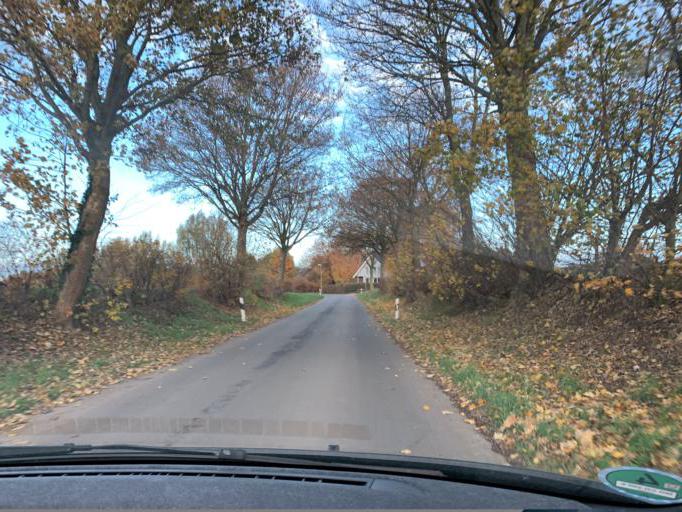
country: DE
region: North Rhine-Westphalia
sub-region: Regierungsbezirk Koln
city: Titz
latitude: 51.0413
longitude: 6.4083
